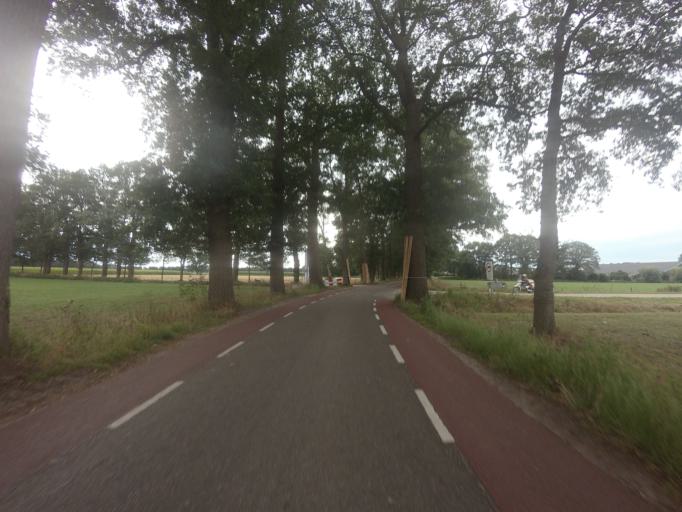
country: NL
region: Overijssel
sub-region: Gemeente Raalte
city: Raalte
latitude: 52.3699
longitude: 6.3049
